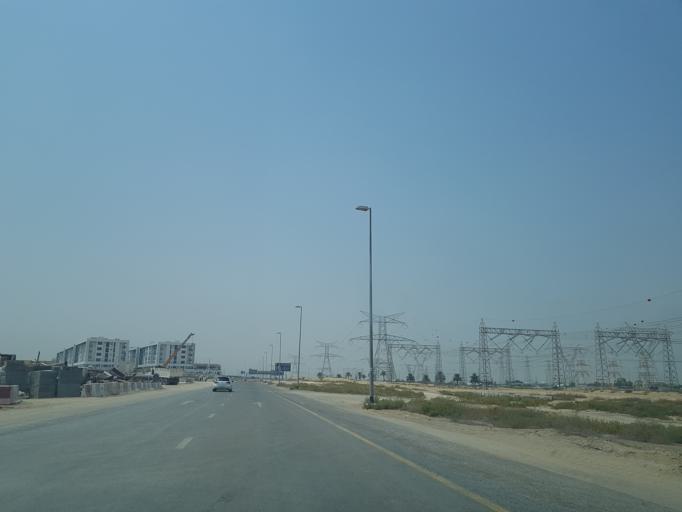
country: AE
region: Ash Shariqah
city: Sharjah
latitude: 25.2246
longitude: 55.4084
